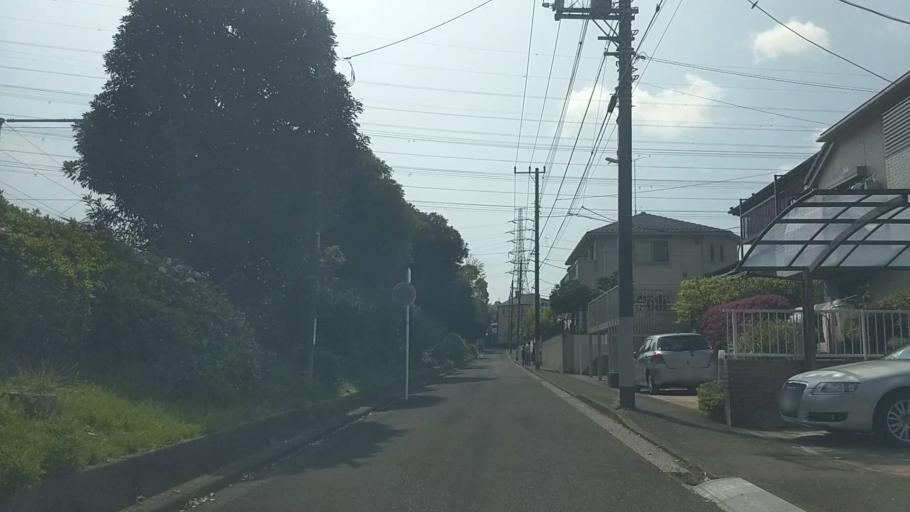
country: JP
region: Kanagawa
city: Kamakura
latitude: 35.3739
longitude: 139.5729
